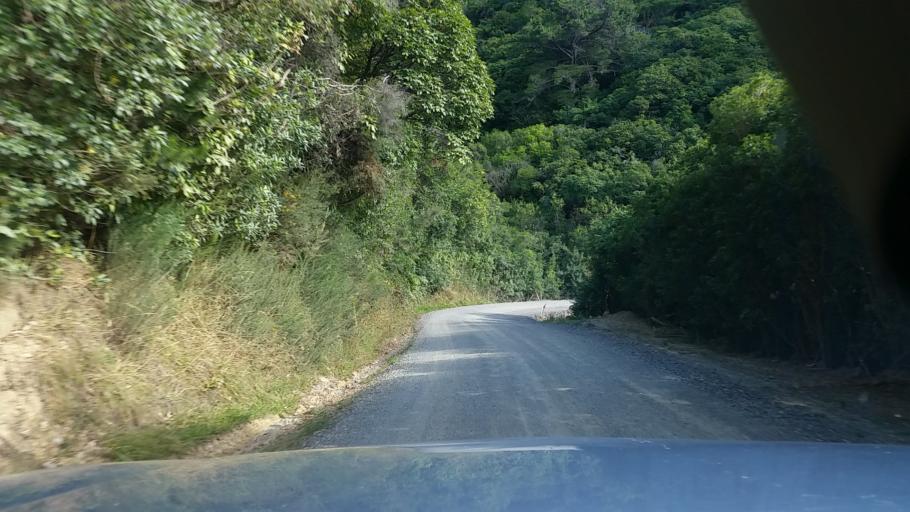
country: NZ
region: Marlborough
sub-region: Marlborough District
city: Picton
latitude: -41.2875
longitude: 174.1304
